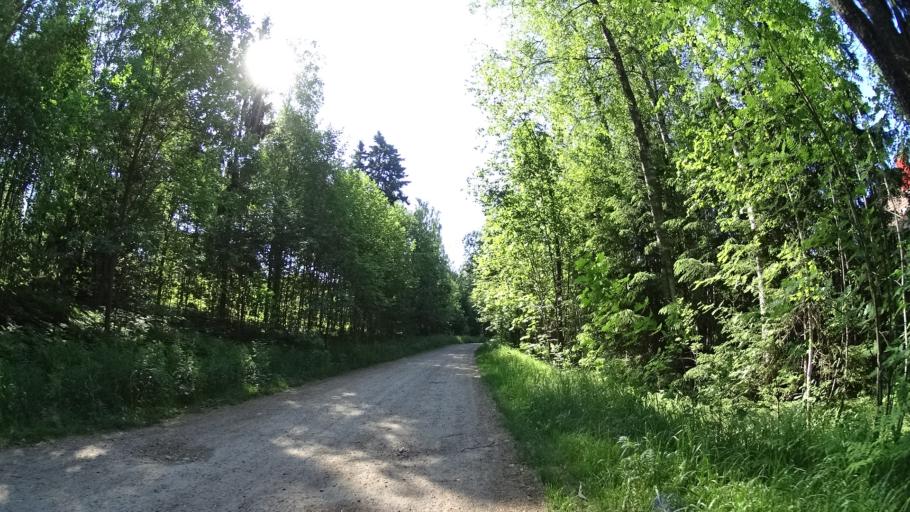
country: FI
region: Uusimaa
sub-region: Helsinki
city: Kilo
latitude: 60.2409
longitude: 24.8011
